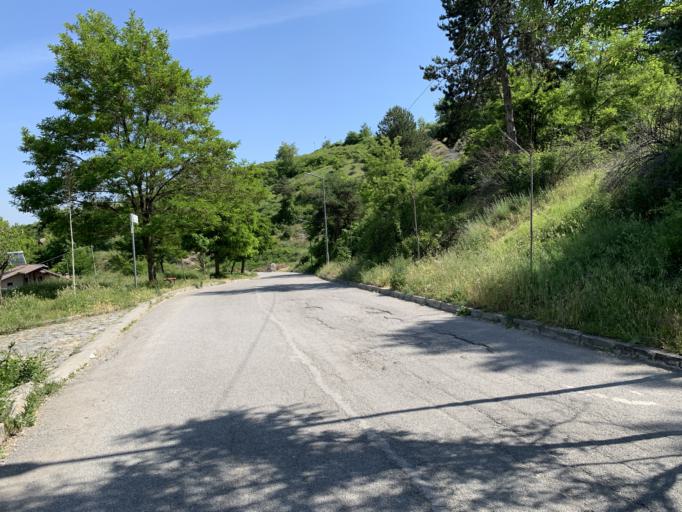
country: AL
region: Korce
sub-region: Rrethi i Korces
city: Korce
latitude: 40.6168
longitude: 20.7877
